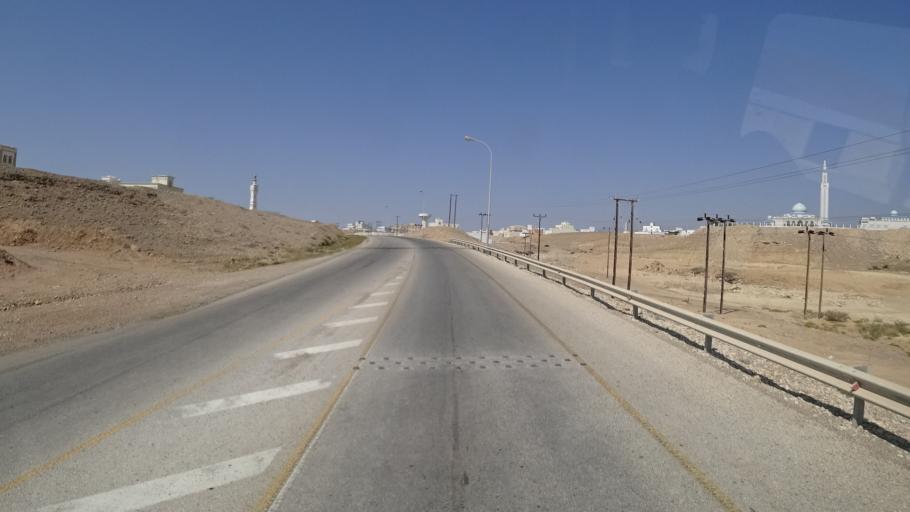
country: OM
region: Ash Sharqiyah
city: Sur
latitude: 22.5592
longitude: 59.5012
